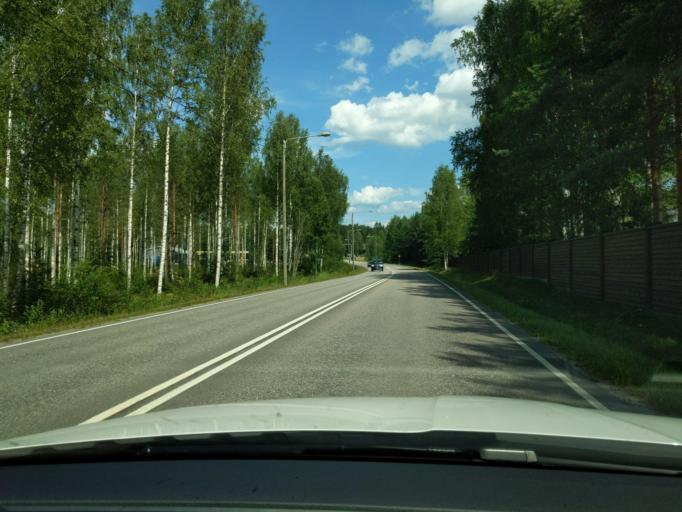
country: FI
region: Paijanne Tavastia
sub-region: Lahti
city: Heinola
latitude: 61.2463
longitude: 26.0550
